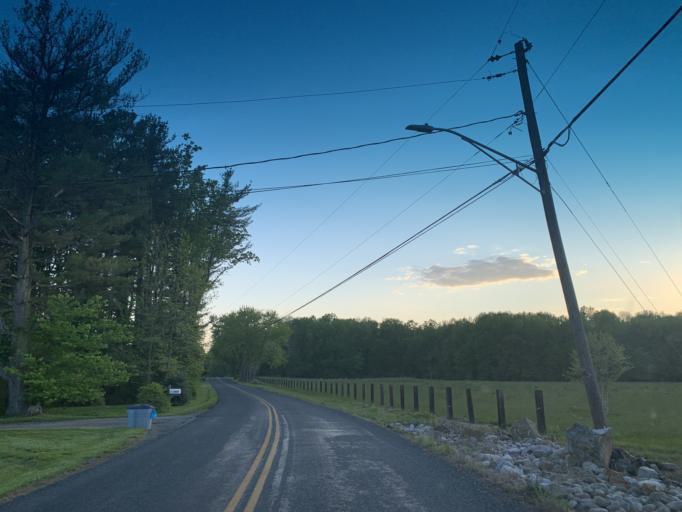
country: US
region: Maryland
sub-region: Harford County
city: Riverside
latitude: 39.5321
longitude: -76.2255
